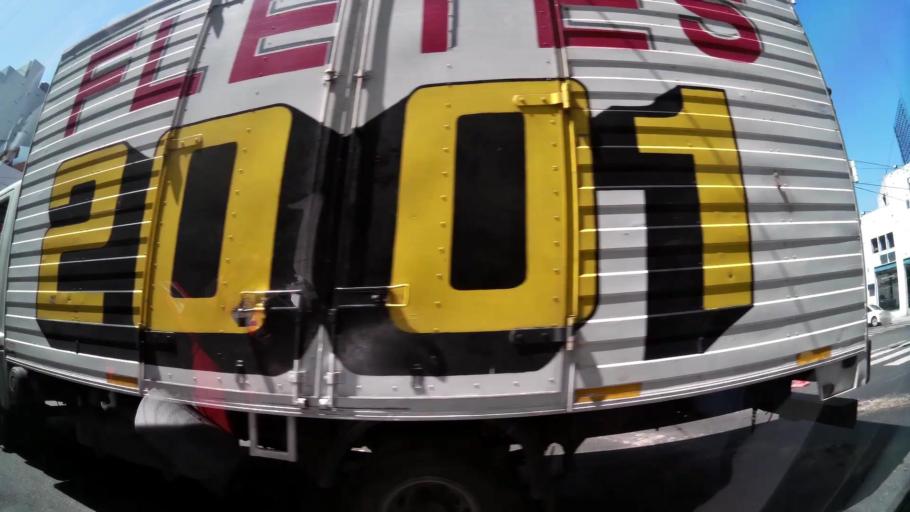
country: AR
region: Buenos Aires F.D.
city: Buenos Aires
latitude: -34.6385
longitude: -58.4130
